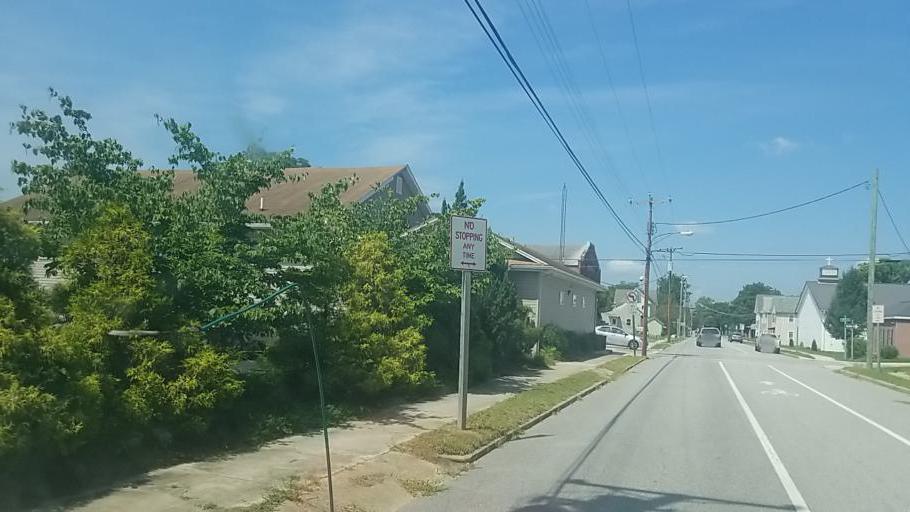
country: US
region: Maryland
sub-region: Caroline County
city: Denton
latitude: 38.8863
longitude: -75.8284
